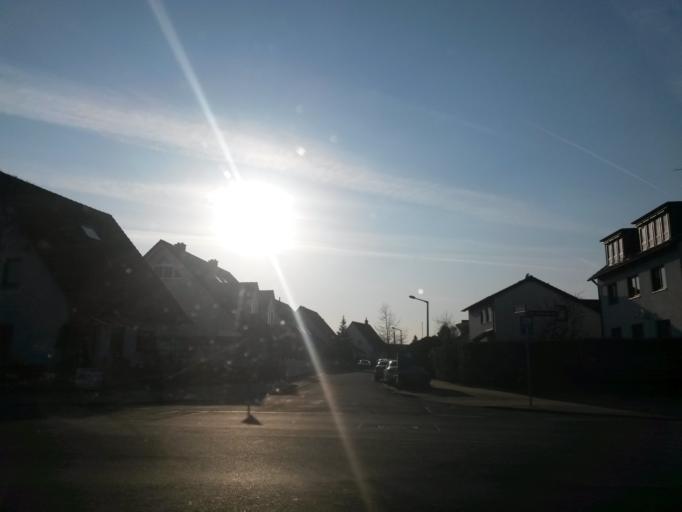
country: DE
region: Bavaria
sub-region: Regierungsbezirk Mittelfranken
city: Furth
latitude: 49.4569
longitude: 11.0044
